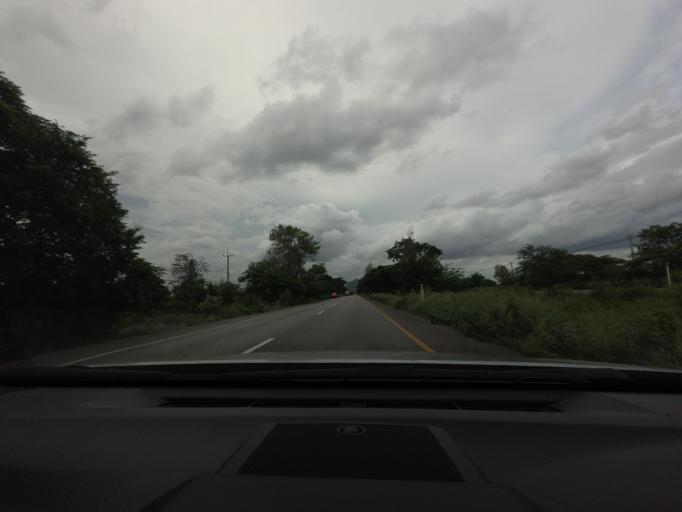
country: TH
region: Phetchaburi
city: Cha-am
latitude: 12.7643
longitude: 99.9342
